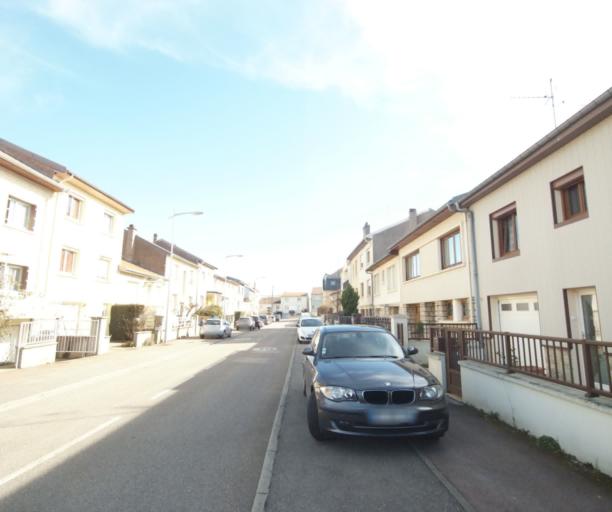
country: FR
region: Lorraine
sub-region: Departement de Meurthe-et-Moselle
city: Villers-les-Nancy
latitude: 48.6638
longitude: 6.1615
